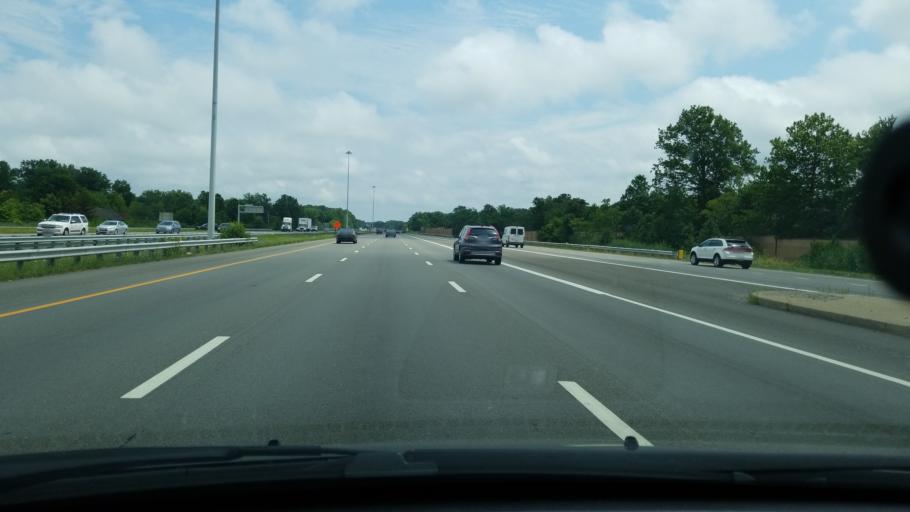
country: US
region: Ohio
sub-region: Cuyahoga County
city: Bay Village
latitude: 41.4681
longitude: -81.9489
